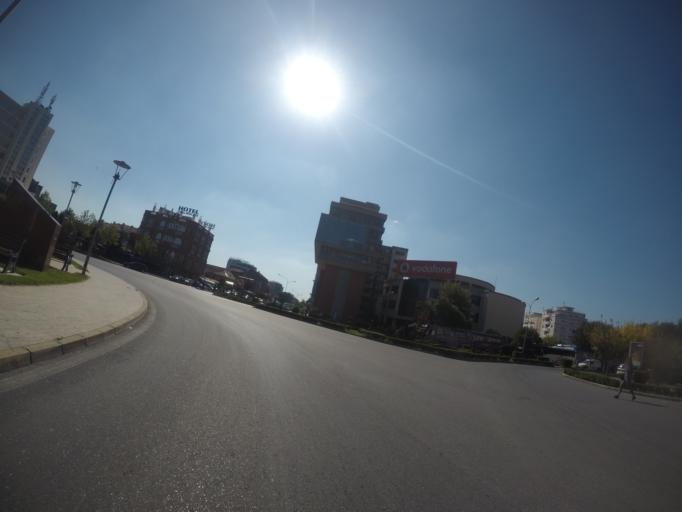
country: AL
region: Shkoder
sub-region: Rrethi i Shkodres
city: Shkoder
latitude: 42.0683
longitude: 19.5120
